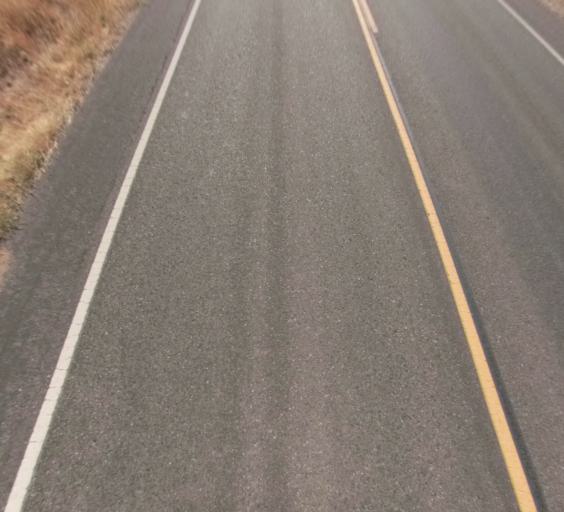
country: US
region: California
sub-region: Madera County
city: Parksdale
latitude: 36.9666
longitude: -119.9539
